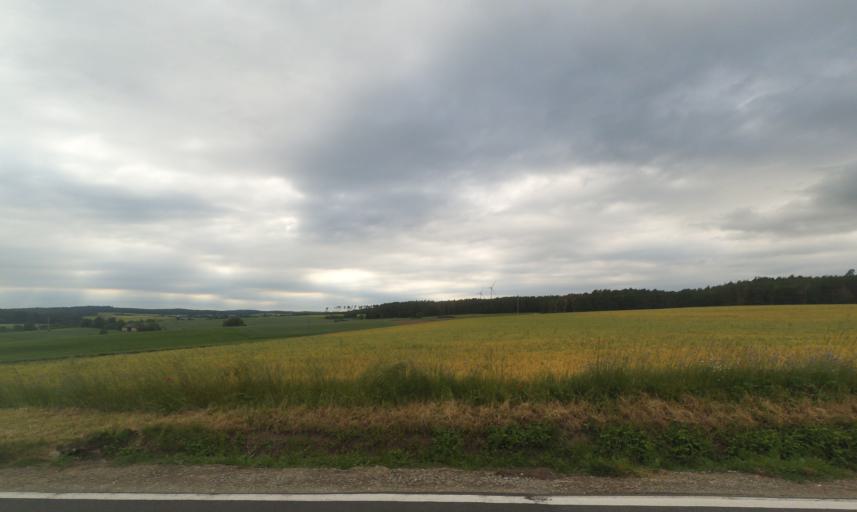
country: DE
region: Bavaria
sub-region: Regierungsbezirk Mittelfranken
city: Burghaslach
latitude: 49.7016
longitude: 10.5894
